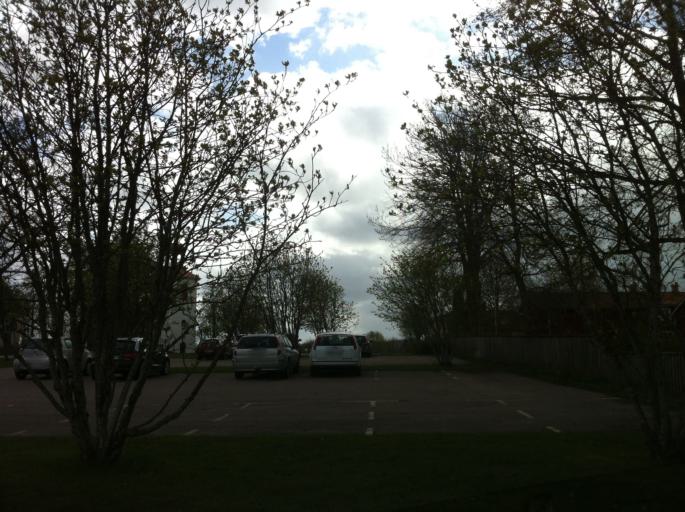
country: SE
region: Vaestra Goetaland
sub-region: Alingsas Kommun
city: Ingared
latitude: 57.8174
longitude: 12.5588
